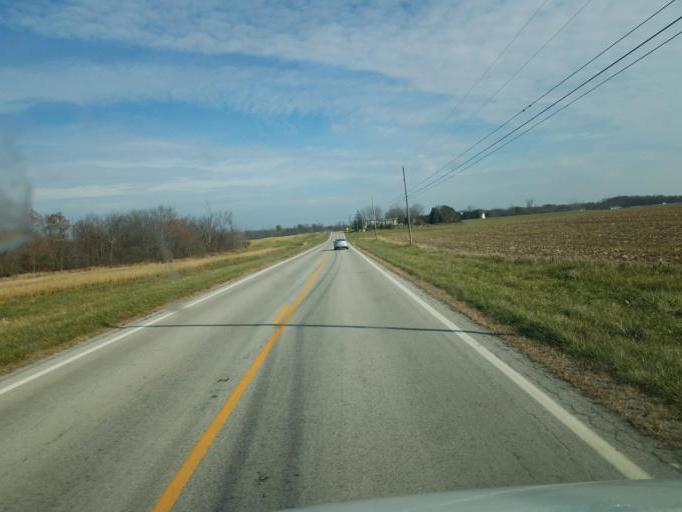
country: US
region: Ohio
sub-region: Hardin County
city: Forest
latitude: 40.7054
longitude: -83.4500
